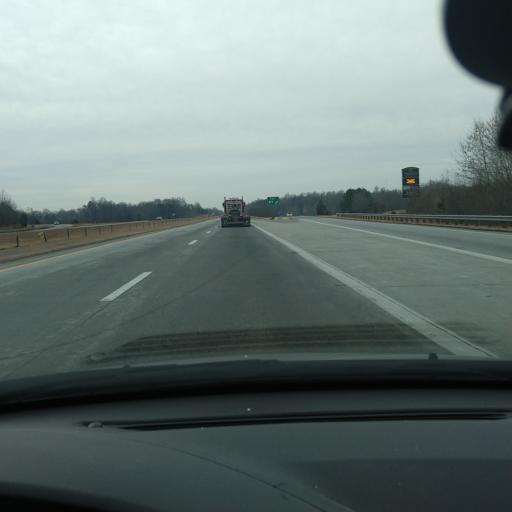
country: US
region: North Carolina
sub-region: Davidson County
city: Lexington
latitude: 35.8409
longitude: -80.2823
